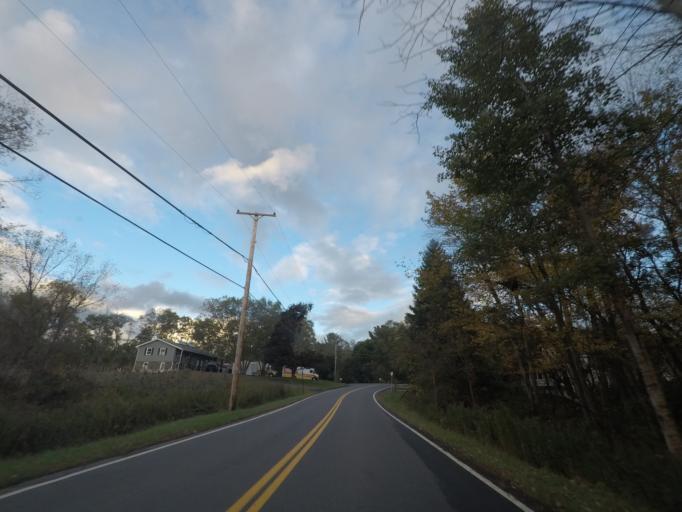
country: US
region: New York
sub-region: Rensselaer County
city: Nassau
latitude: 42.5566
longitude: -73.6208
